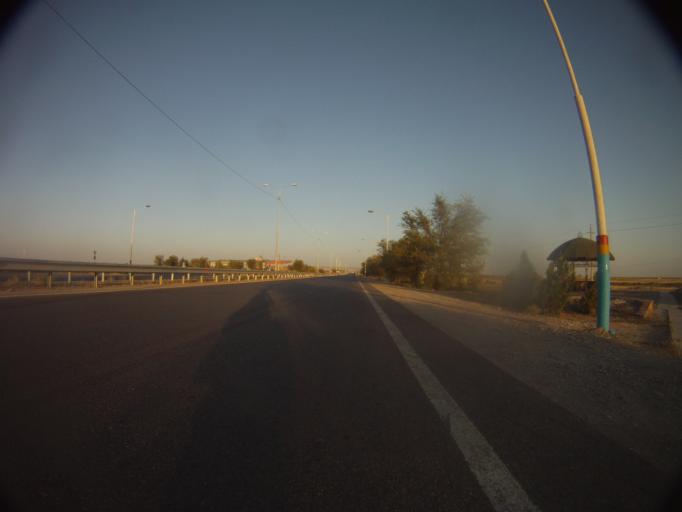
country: KZ
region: Ongtustik Qazaqstan
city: Turkestan
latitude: 43.2765
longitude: 68.3318
